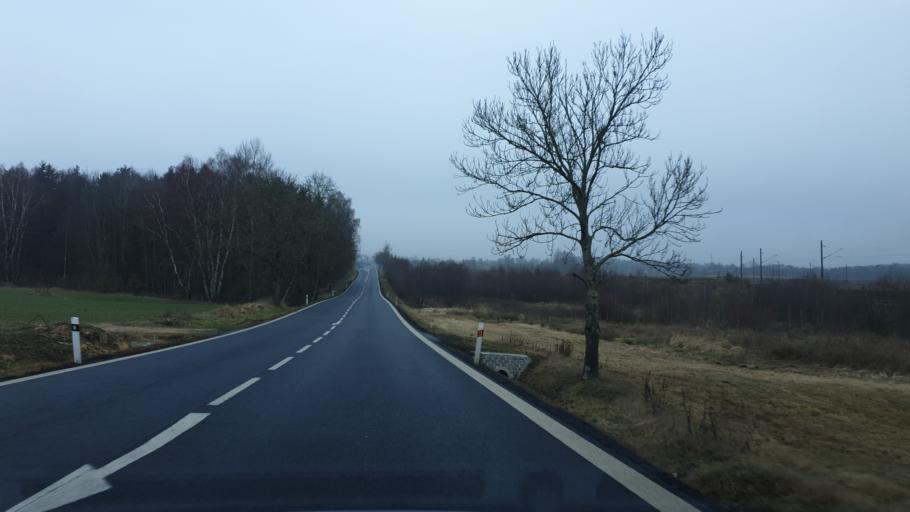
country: CZ
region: Karlovarsky
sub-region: Okres Cheb
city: Skalna
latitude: 50.1581
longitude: 12.3226
